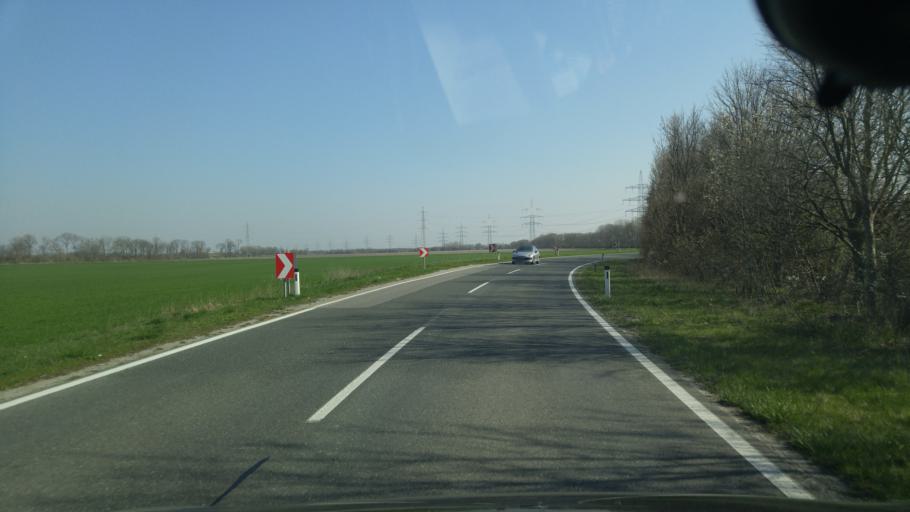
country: AT
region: Lower Austria
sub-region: Politischer Bezirk Baden
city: Trumau
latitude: 47.9984
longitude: 16.3693
